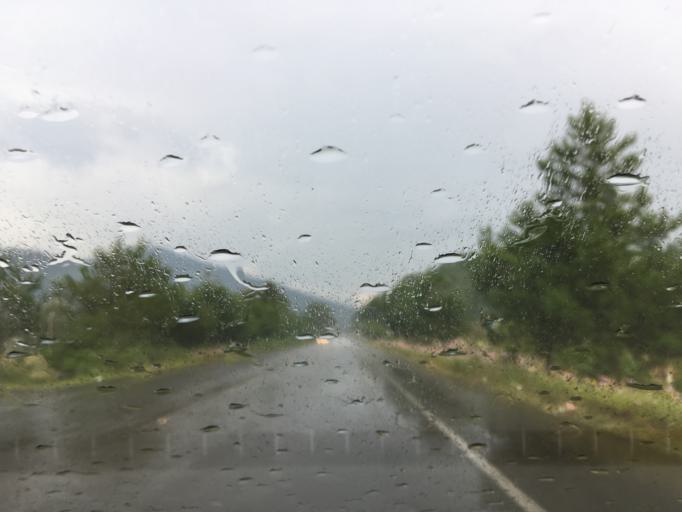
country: MX
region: Michoacan
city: Angahuan
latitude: 19.5646
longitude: -102.2379
